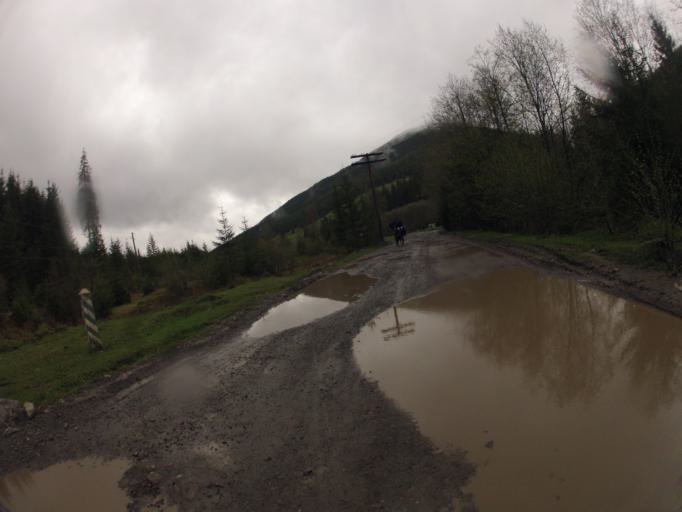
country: RO
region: Suceava
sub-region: Comuna Izvoarele Sucevei
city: Izvoarele Sucevei
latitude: 47.8323
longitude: 25.0573
